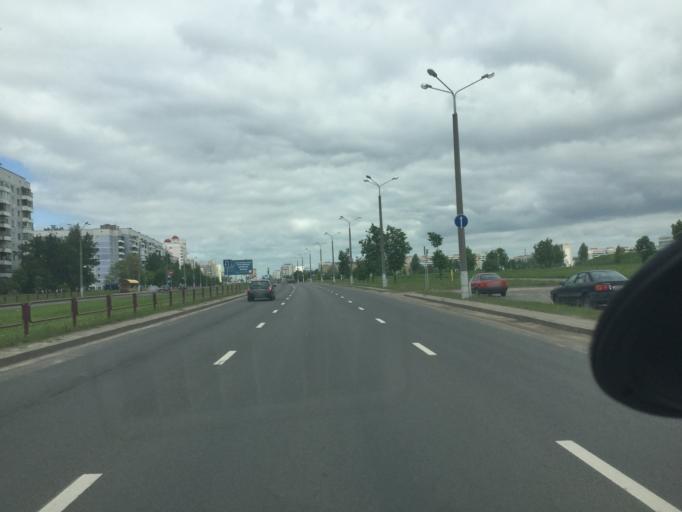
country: BY
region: Vitebsk
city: Vitebsk
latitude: 55.1632
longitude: 30.2226
